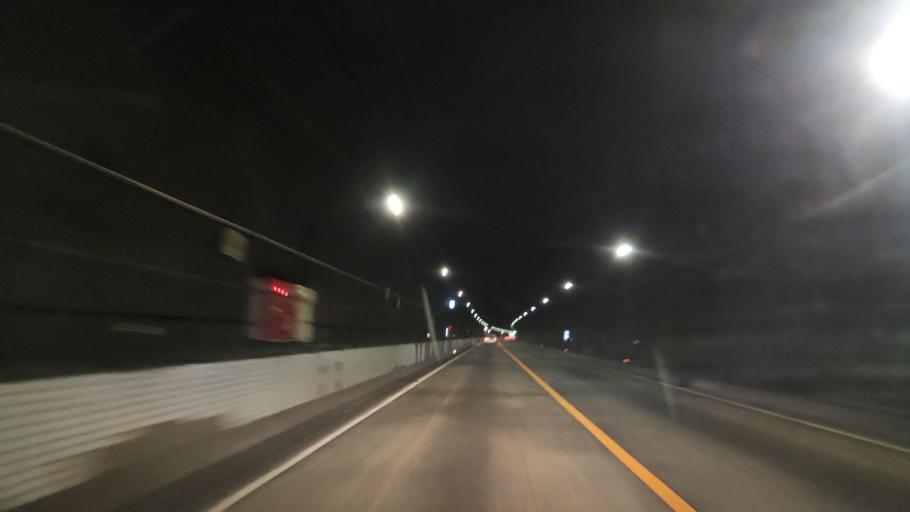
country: JP
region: Okayama
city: Okayama-shi
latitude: 34.7138
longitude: 133.9256
